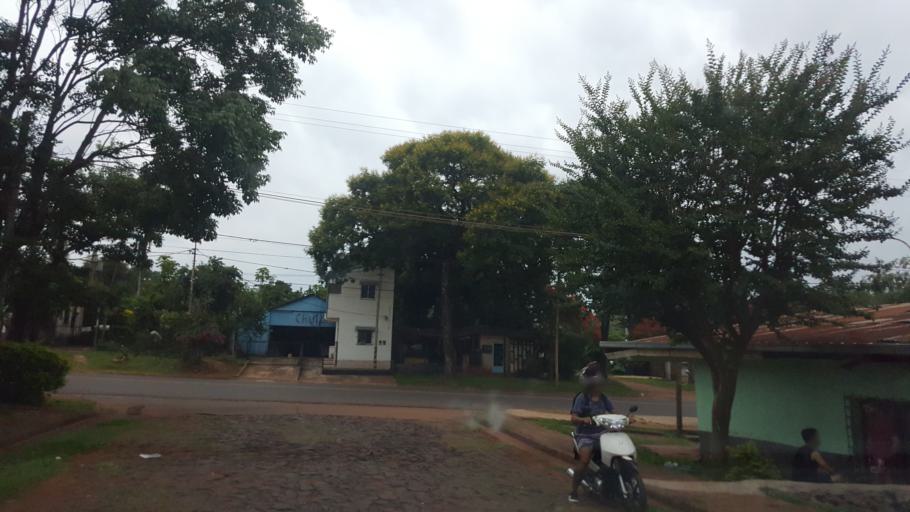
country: AR
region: Misiones
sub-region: Departamento de Capital
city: Posadas
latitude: -27.3671
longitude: -55.9298
